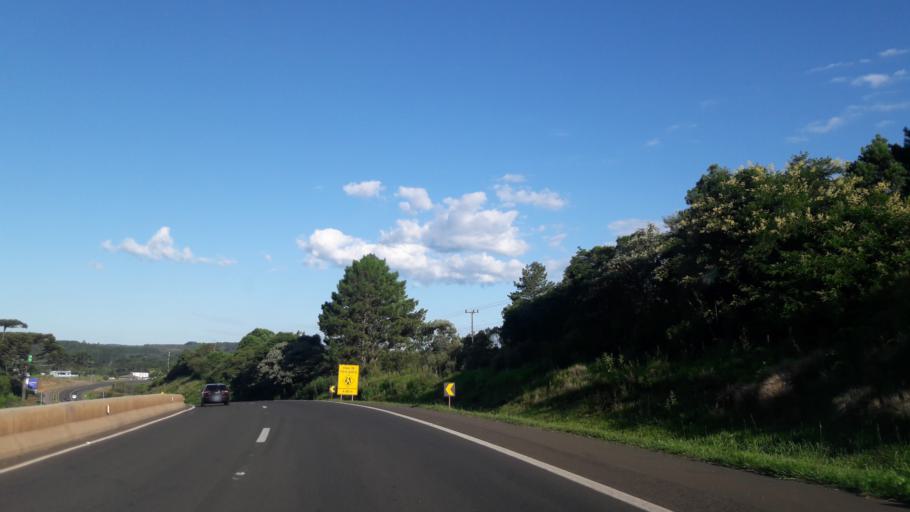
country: BR
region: Parana
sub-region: Guarapuava
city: Guarapuava
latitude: -25.3534
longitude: -51.3729
